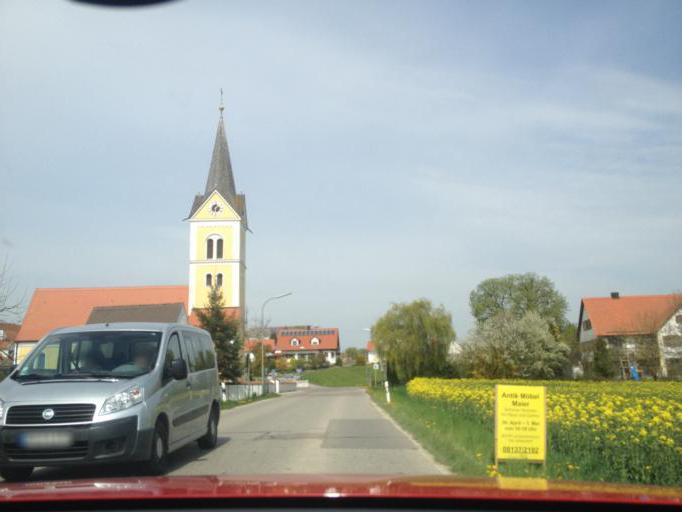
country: DE
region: Bavaria
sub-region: Upper Bavaria
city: Paunzhausen
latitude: 48.4954
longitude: 11.5825
